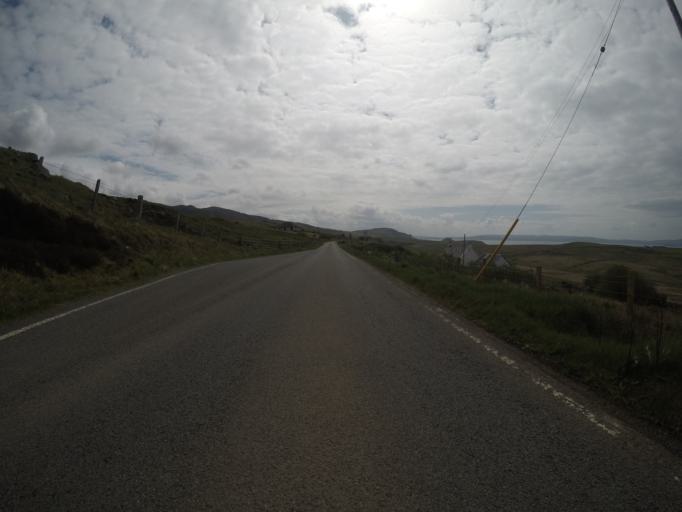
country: GB
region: Scotland
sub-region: Highland
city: Portree
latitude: 57.6258
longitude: -6.3774
